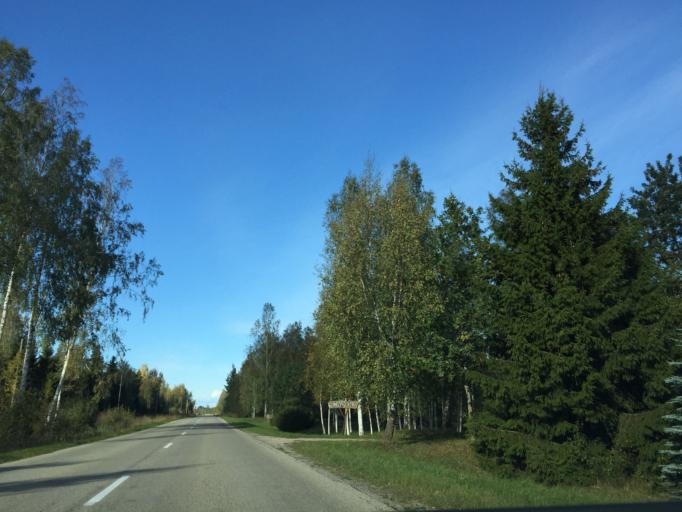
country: LV
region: Rojas
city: Roja
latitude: 57.4354
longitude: 22.9084
